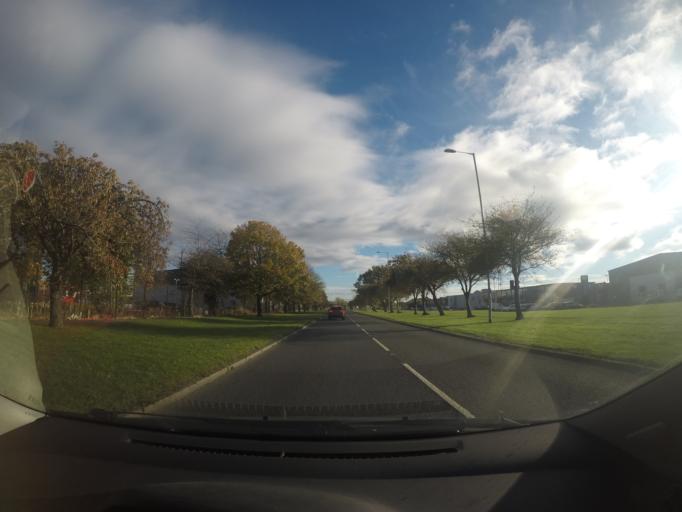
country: GB
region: England
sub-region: City and Borough of Leeds
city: Shadwell
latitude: 53.8296
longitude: -1.4612
